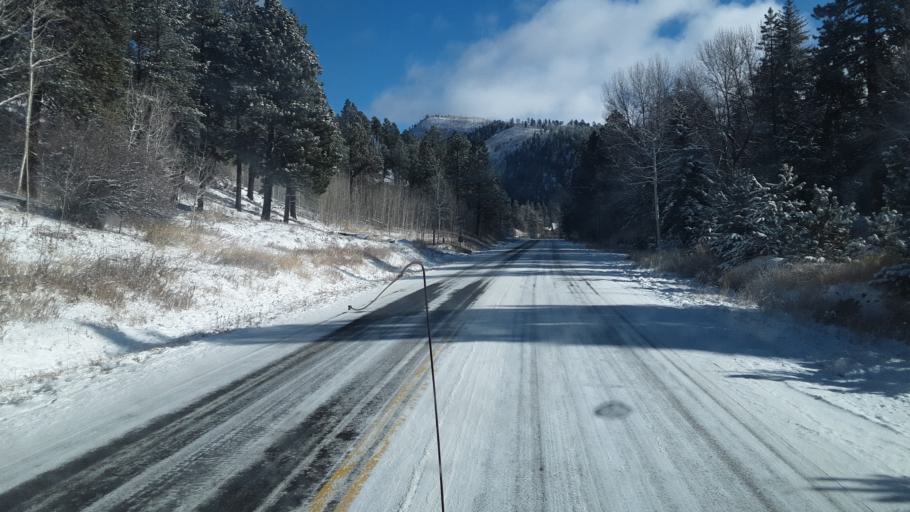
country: US
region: Colorado
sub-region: La Plata County
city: Bayfield
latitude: 37.3582
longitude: -107.6769
